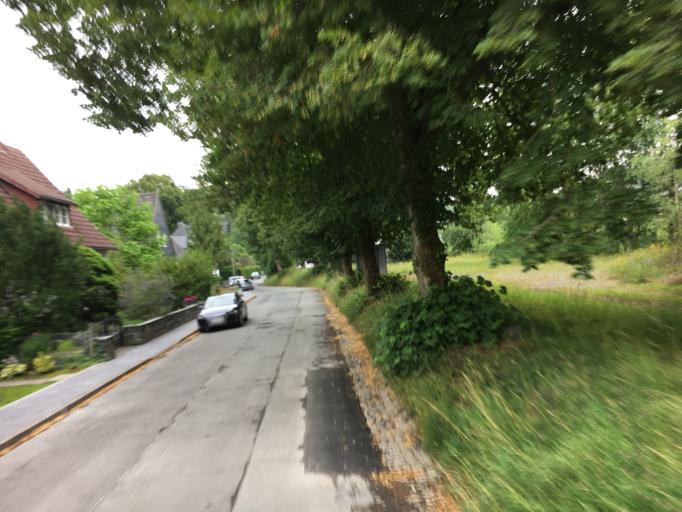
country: DE
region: North Rhine-Westphalia
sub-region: Regierungsbezirk Arnsberg
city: Bad Laasphe
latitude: 50.9226
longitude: 8.4003
